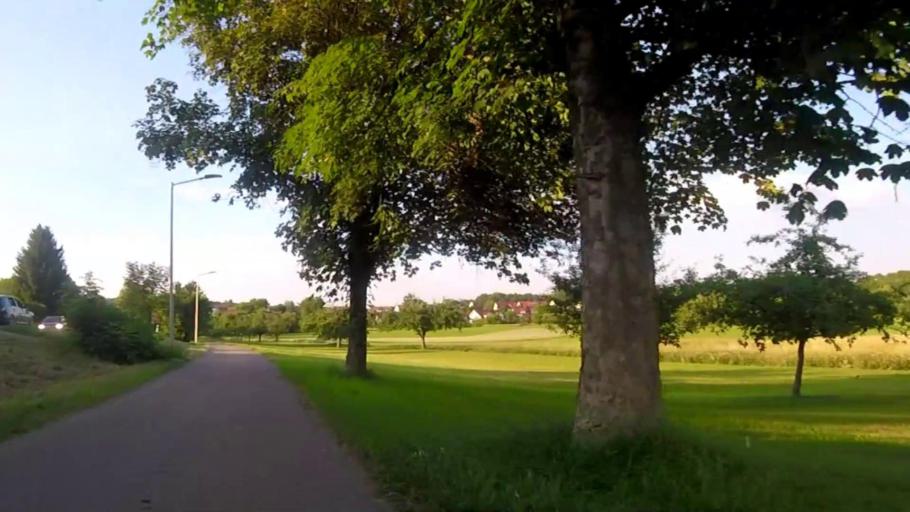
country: DE
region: Baden-Wuerttemberg
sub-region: Regierungsbezirk Stuttgart
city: Backnang
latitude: 48.9701
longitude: 9.4378
